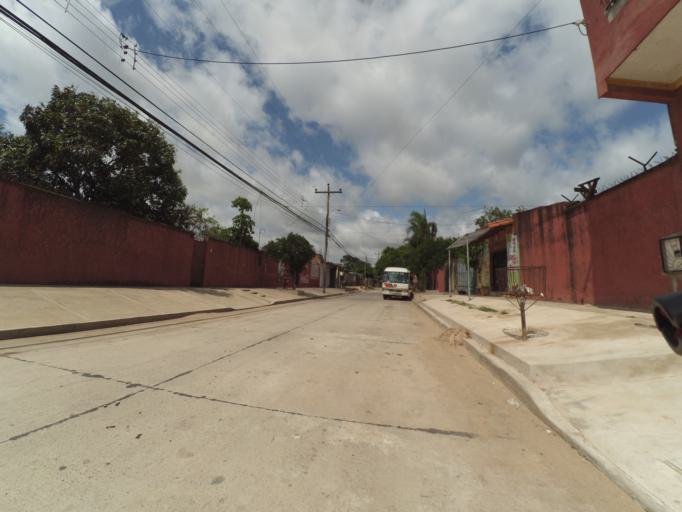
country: BO
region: Santa Cruz
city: Santa Cruz de la Sierra
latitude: -17.7961
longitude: -63.2187
